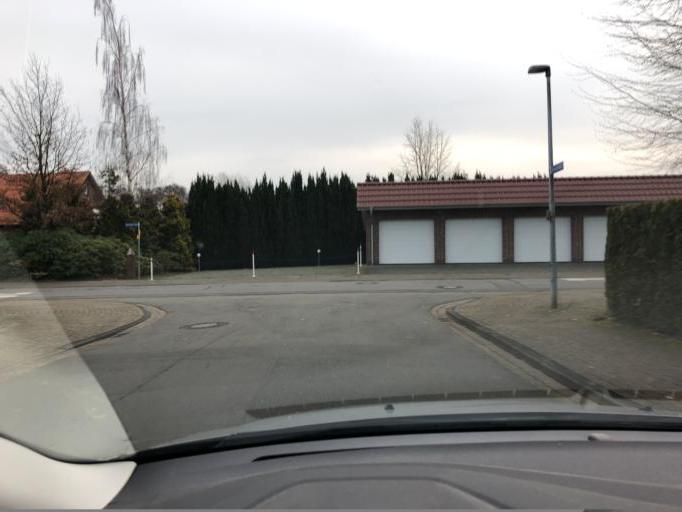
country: DE
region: Lower Saxony
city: Bad Zwischenahn
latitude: 53.1790
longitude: 8.0123
